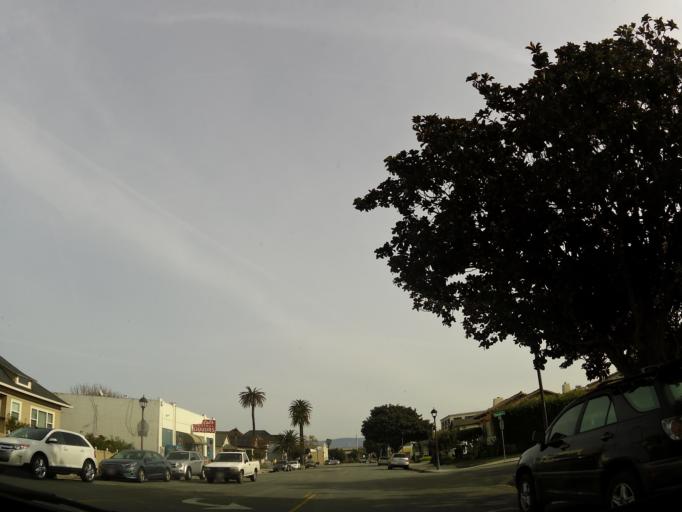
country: US
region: California
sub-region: Monterey County
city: Salinas
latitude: 36.6764
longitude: -121.6591
